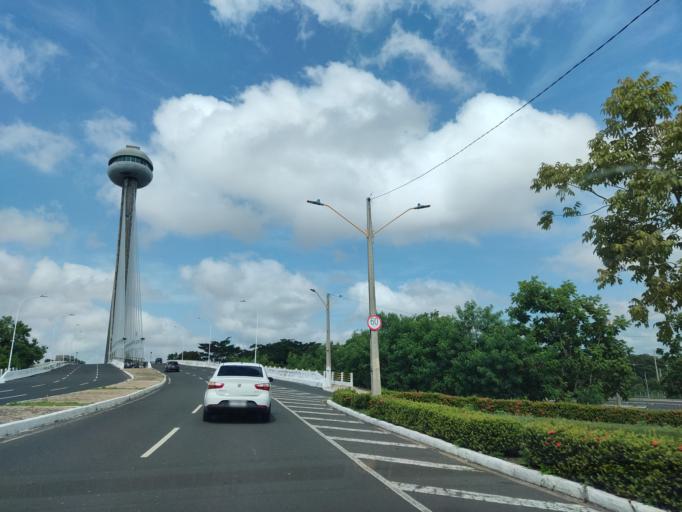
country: BR
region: Piaui
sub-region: Teresina
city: Teresina
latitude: -5.0693
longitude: -42.8007
